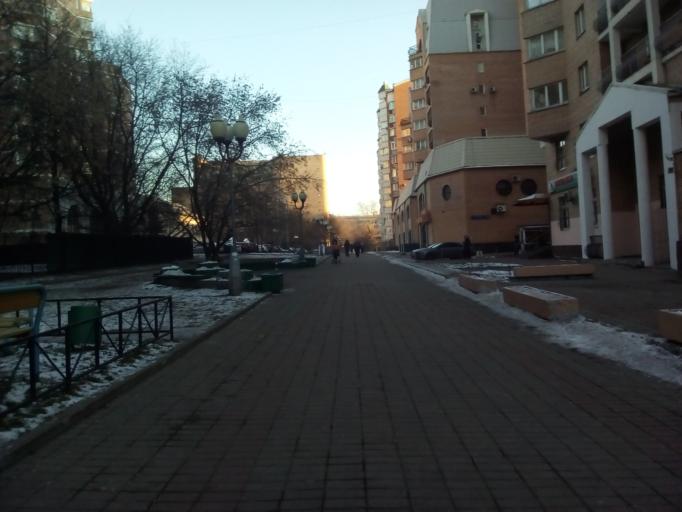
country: RU
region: Moskovskaya
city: Dorogomilovo
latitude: 55.7661
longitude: 37.5808
